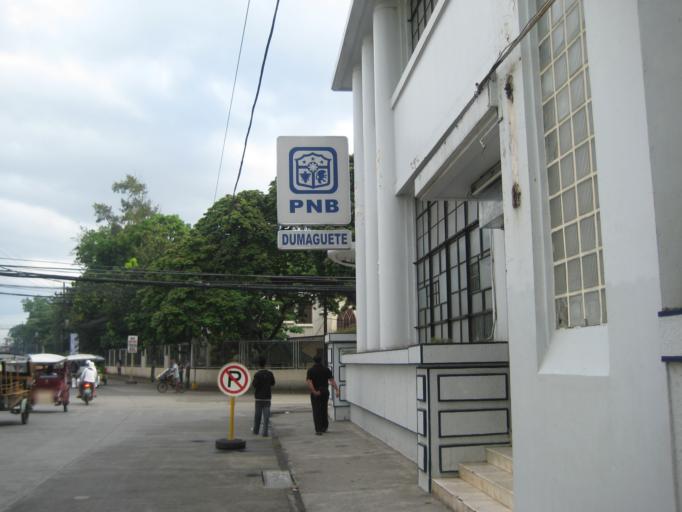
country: PH
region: Central Visayas
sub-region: Province of Negros Oriental
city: Dumaguete
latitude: 9.3096
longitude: 123.3057
